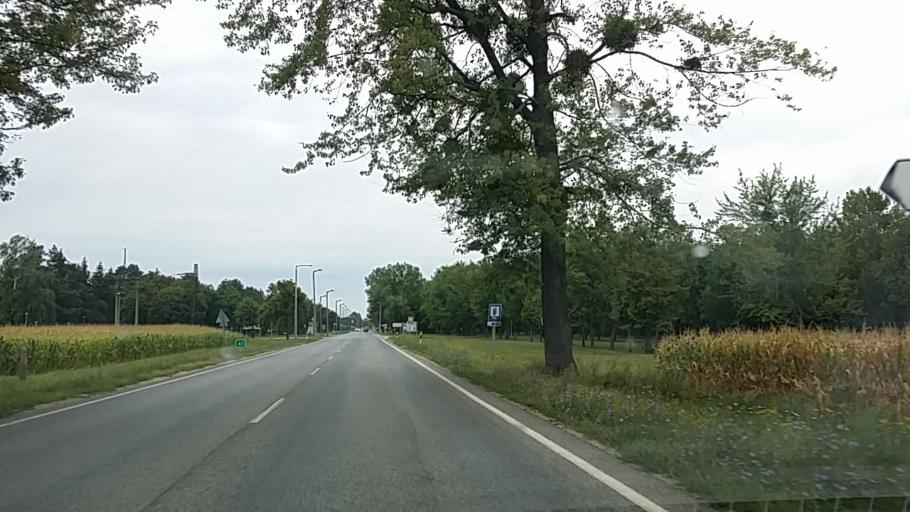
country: HU
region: Gyor-Moson-Sopron
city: Kapuvar
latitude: 47.5911
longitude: 17.0455
